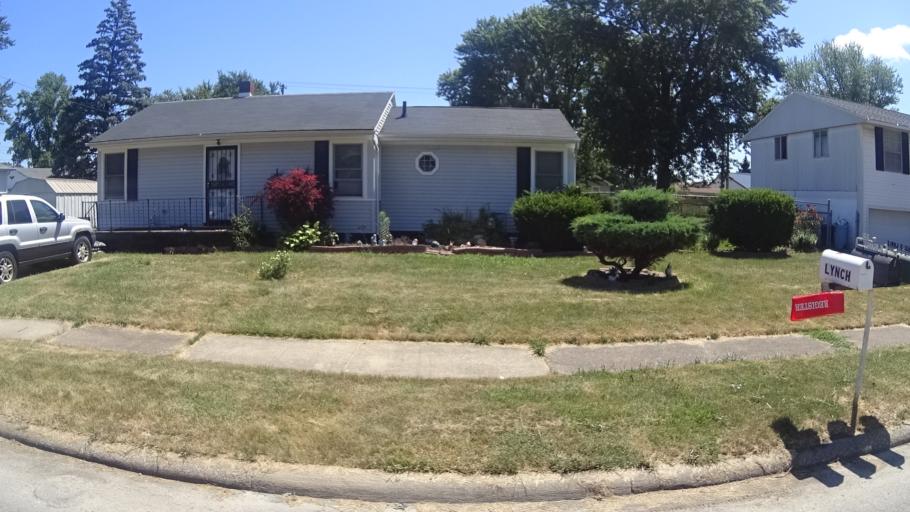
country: US
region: Ohio
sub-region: Erie County
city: Sandusky
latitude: 41.4359
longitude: -82.7354
